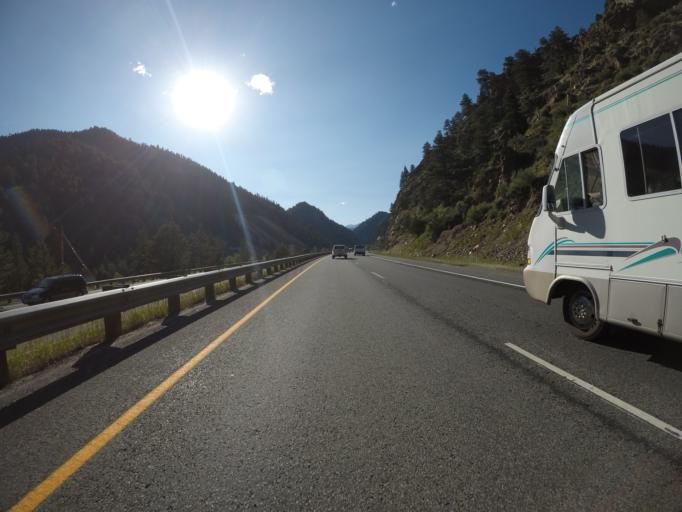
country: US
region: Colorado
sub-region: Clear Creek County
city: Idaho Springs
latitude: 39.7476
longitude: -105.5455
